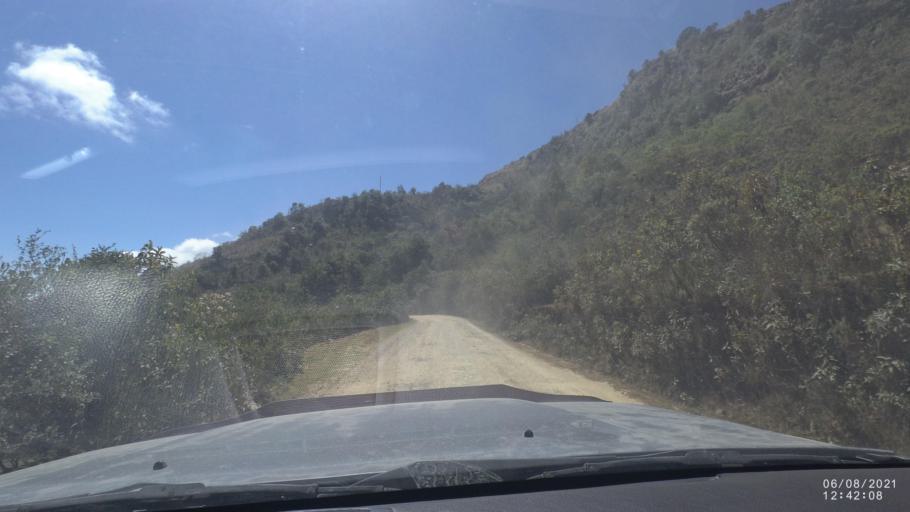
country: BO
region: Cochabamba
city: Colchani
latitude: -16.7793
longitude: -66.6658
